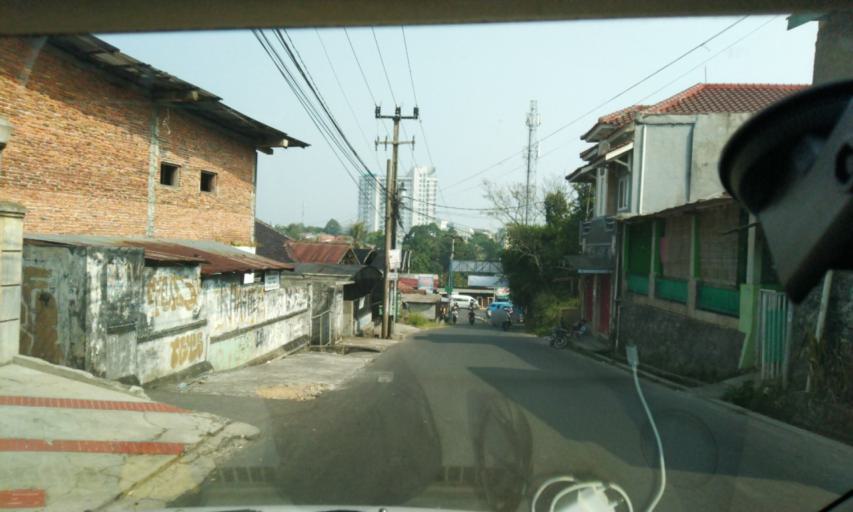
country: ID
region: West Java
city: Caringin
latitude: -6.6615
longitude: 106.8578
